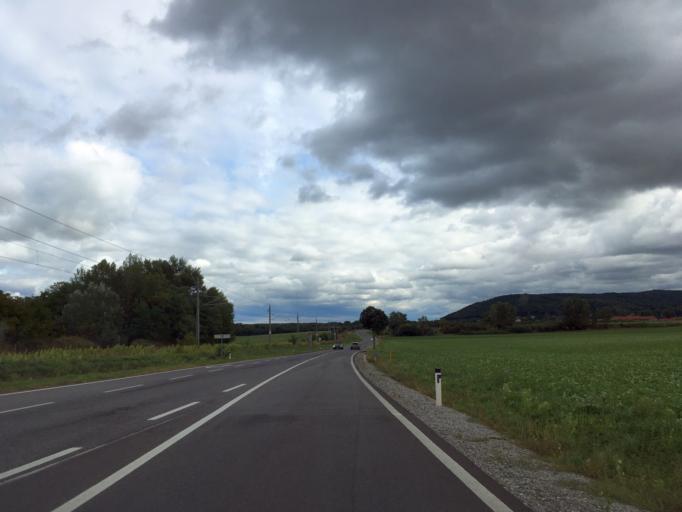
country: AT
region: Lower Austria
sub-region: Politischer Bezirk Bruck an der Leitha
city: Wolfsthal
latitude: 48.1428
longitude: 16.9817
